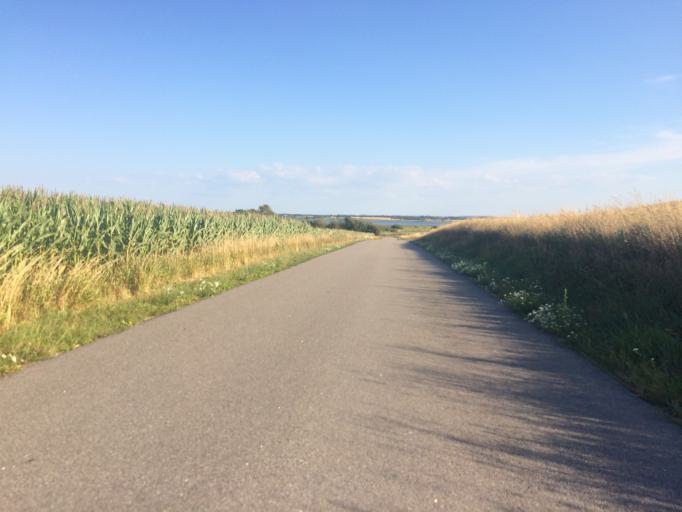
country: DK
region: Central Jutland
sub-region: Holstebro Kommune
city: Vinderup
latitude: 56.5761
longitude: 8.7923
